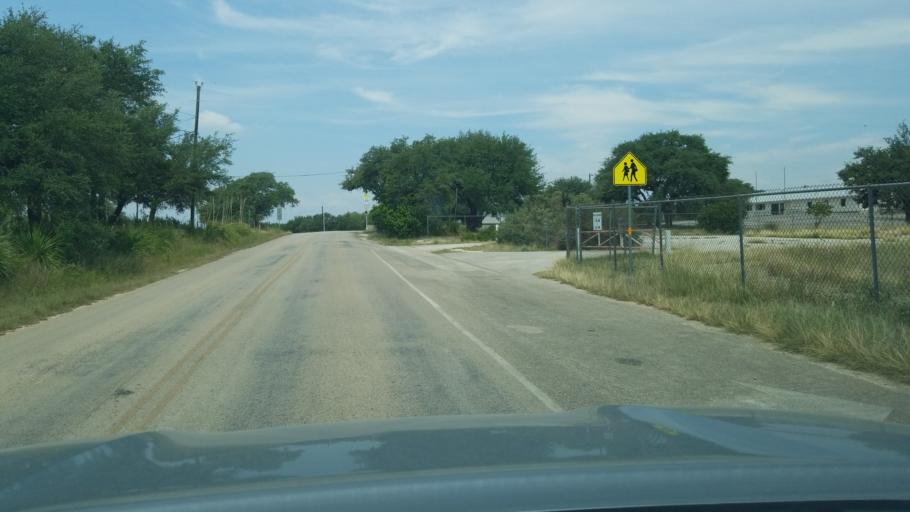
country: US
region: Texas
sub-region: Comal County
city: Bulverde
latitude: 29.7597
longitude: -98.4596
